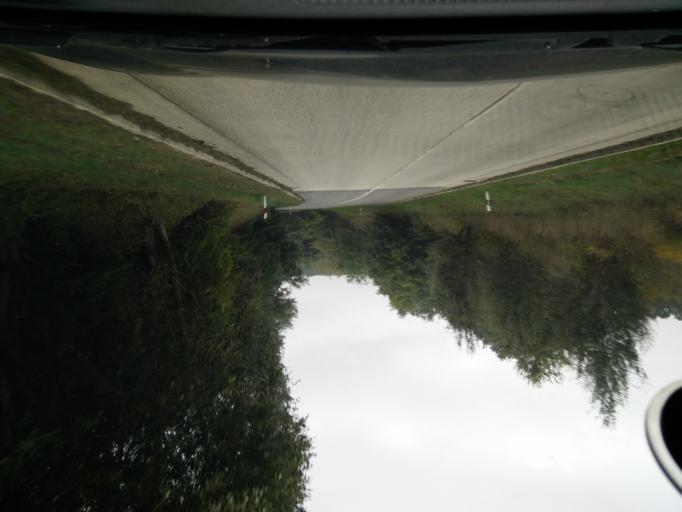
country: HU
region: Komarom-Esztergom
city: Tarjan
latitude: 47.5955
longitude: 18.4899
